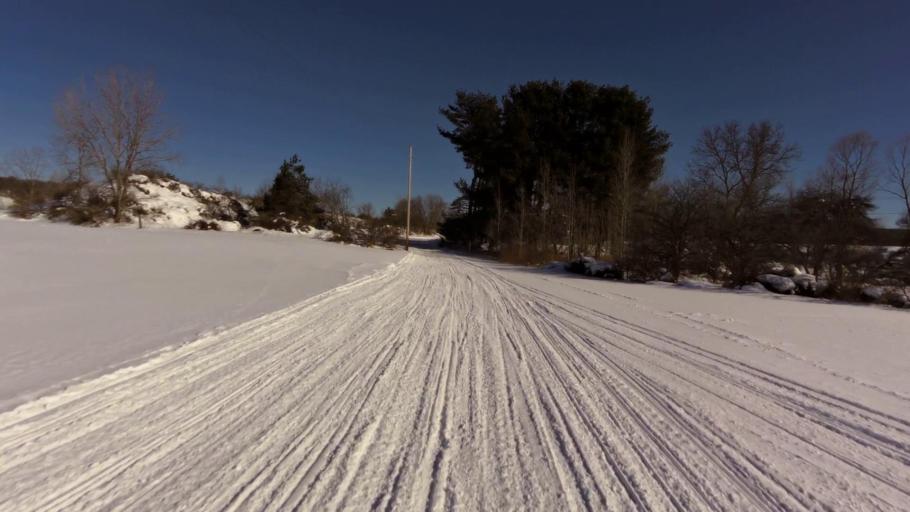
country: US
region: New York
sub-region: Cattaraugus County
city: Franklinville
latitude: 42.3685
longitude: -78.4647
